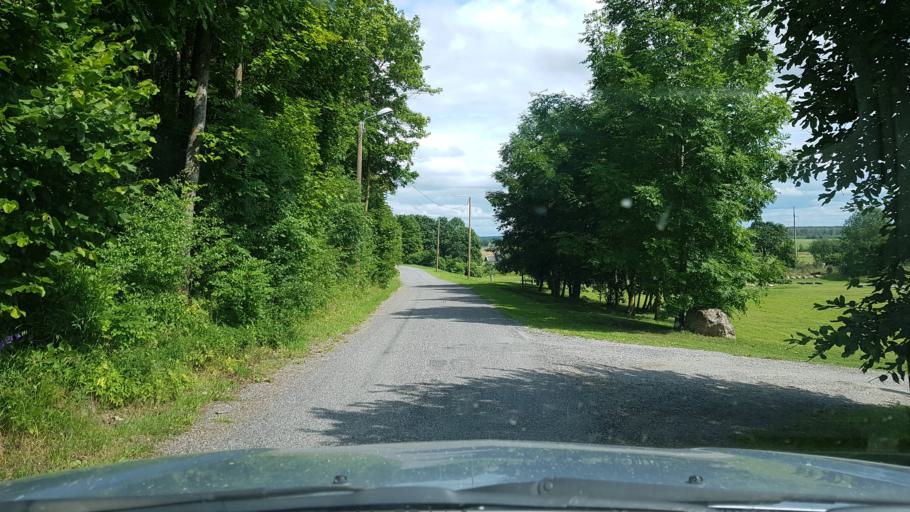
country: EE
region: Ida-Virumaa
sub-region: Sillamaee linn
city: Sillamae
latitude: 59.3724
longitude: 27.8809
